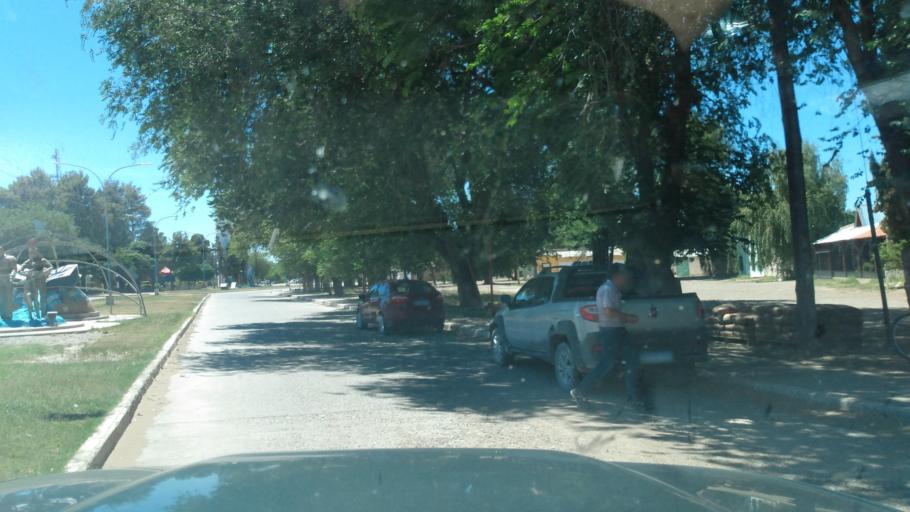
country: AR
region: Neuquen
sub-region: Departamento de Picun Leufu
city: Picun Leufu
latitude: -39.5182
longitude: -69.2935
